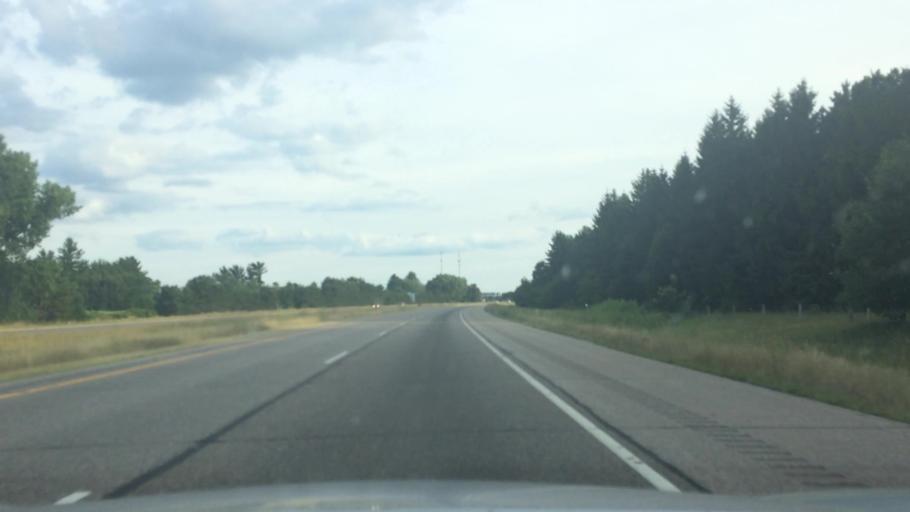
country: US
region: Wisconsin
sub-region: Portage County
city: Plover
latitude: 44.1982
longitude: -89.5230
